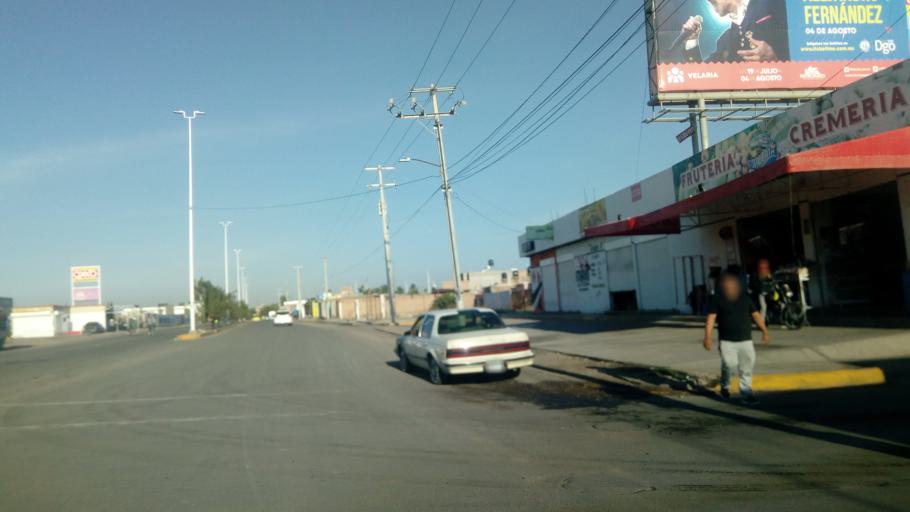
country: MX
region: Durango
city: Victoria de Durango
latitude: 24.0571
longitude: -104.5867
